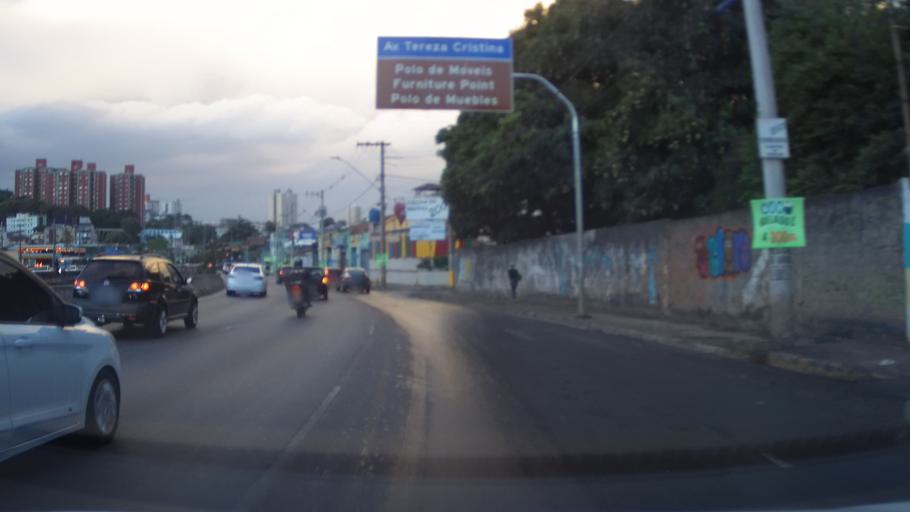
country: BR
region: Minas Gerais
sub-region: Belo Horizonte
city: Belo Horizonte
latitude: -19.9214
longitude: -43.9701
